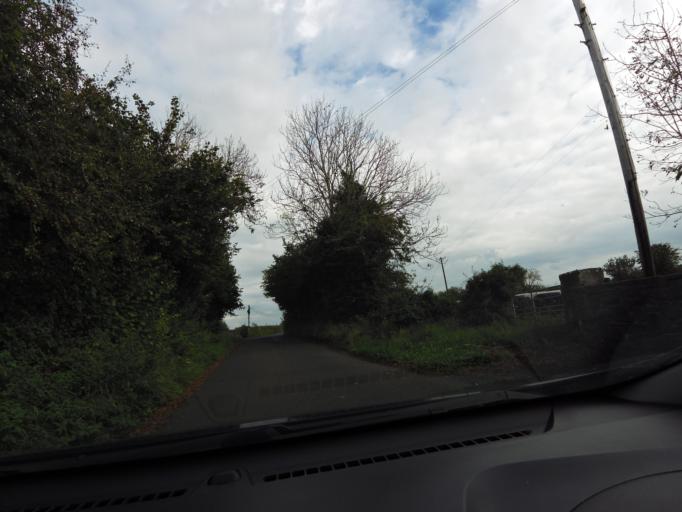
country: IE
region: Connaught
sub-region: County Galway
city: Athenry
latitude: 53.2398
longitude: -8.7350
